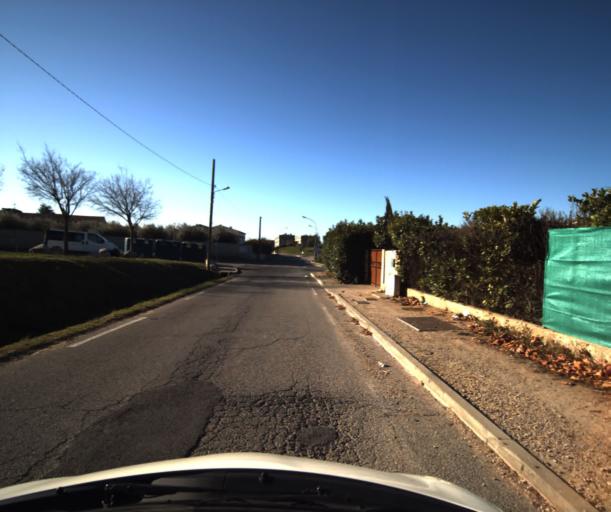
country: FR
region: Provence-Alpes-Cote d'Azur
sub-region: Departement du Vaucluse
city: Pertuis
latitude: 43.6987
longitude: 5.5158
